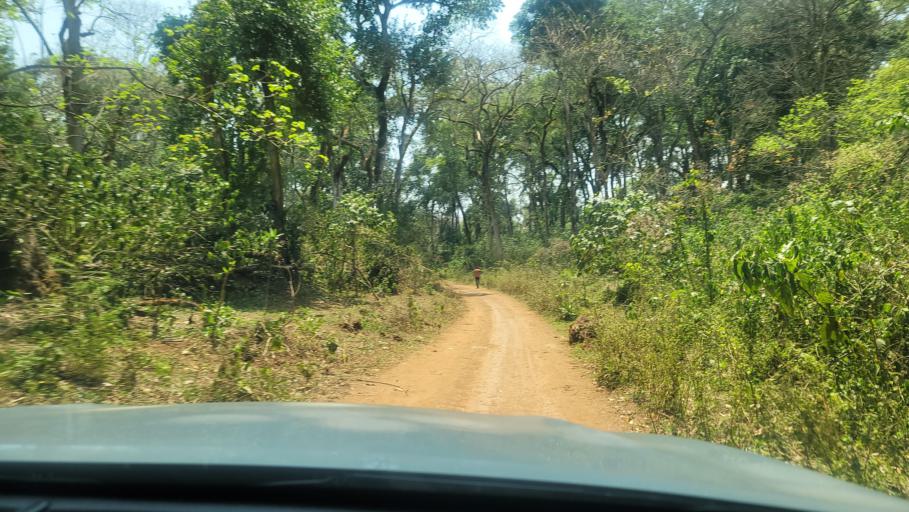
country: ET
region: Southern Nations, Nationalities, and People's Region
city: Bonga
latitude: 7.5090
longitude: 36.2244
